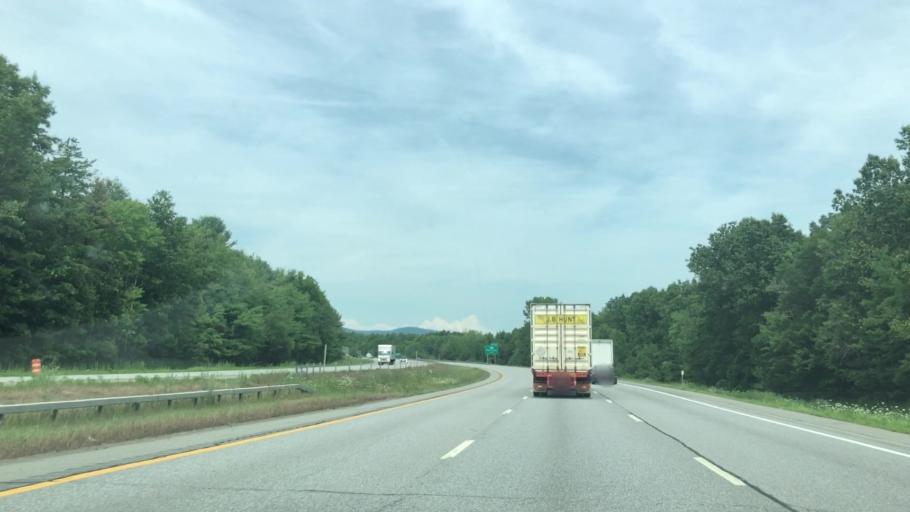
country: US
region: New York
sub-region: Warren County
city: West Glens Falls
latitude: 43.3118
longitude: -73.6751
